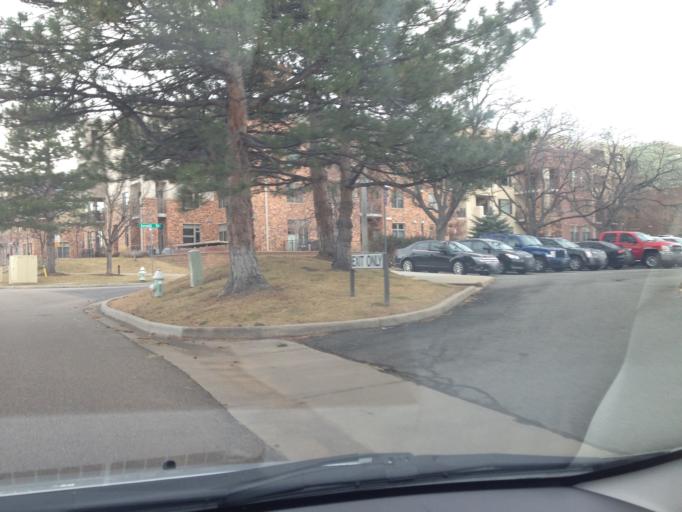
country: US
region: Colorado
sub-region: Boulder County
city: Boulder
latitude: 40.0164
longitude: -105.2470
